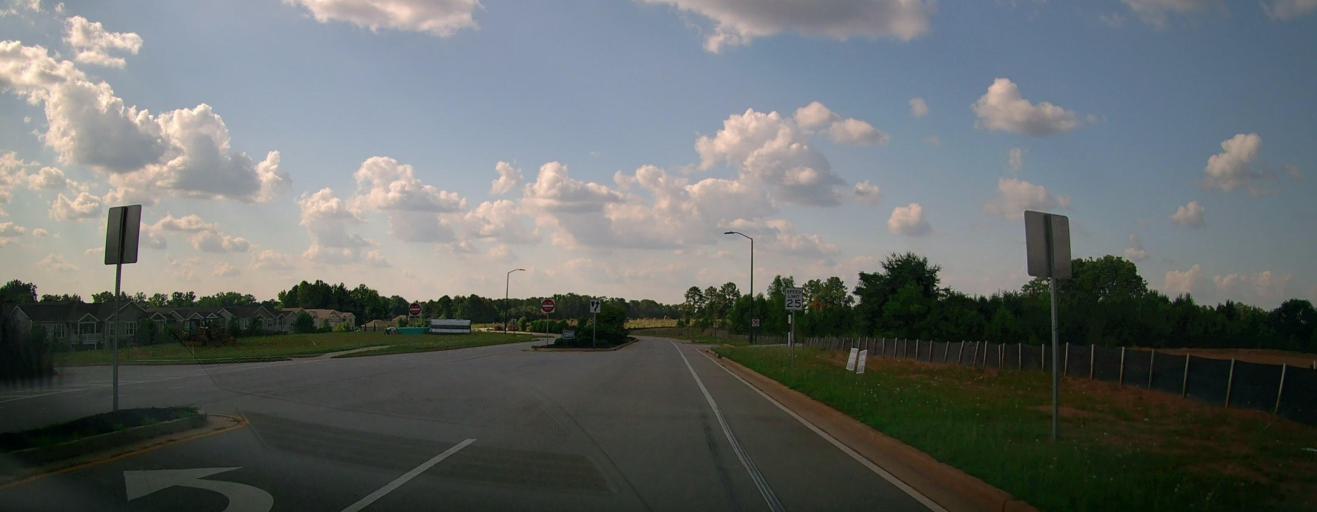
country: US
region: Georgia
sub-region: Henry County
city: McDonough
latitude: 33.4261
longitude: -84.1913
